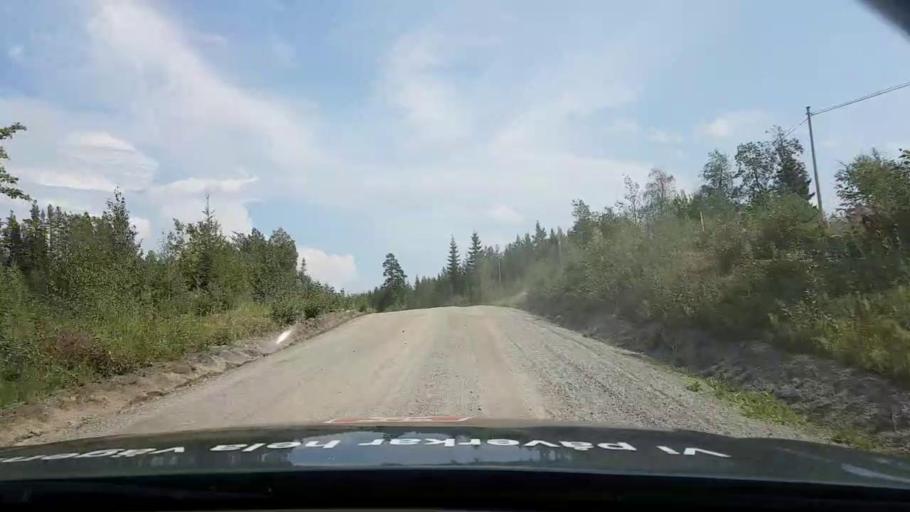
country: SE
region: Jaemtland
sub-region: Braecke Kommun
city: Braecke
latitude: 62.7398
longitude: 15.4409
